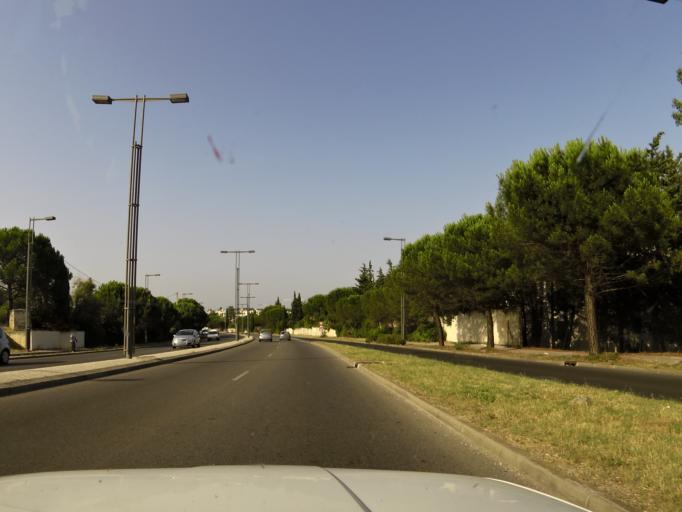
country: FR
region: Languedoc-Roussillon
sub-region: Departement de l'Herault
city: Juvignac
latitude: 43.6274
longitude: 3.8399
